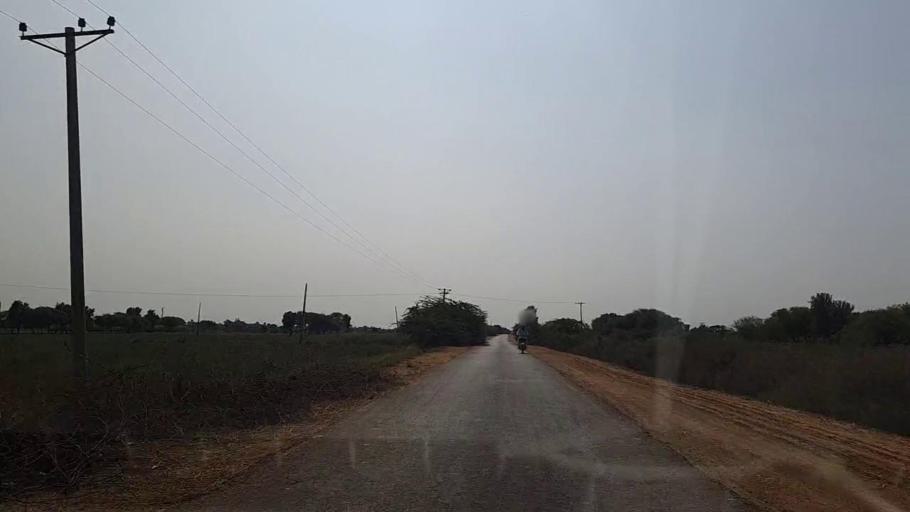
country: PK
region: Sindh
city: Chuhar Jamali
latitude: 24.3188
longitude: 67.9406
